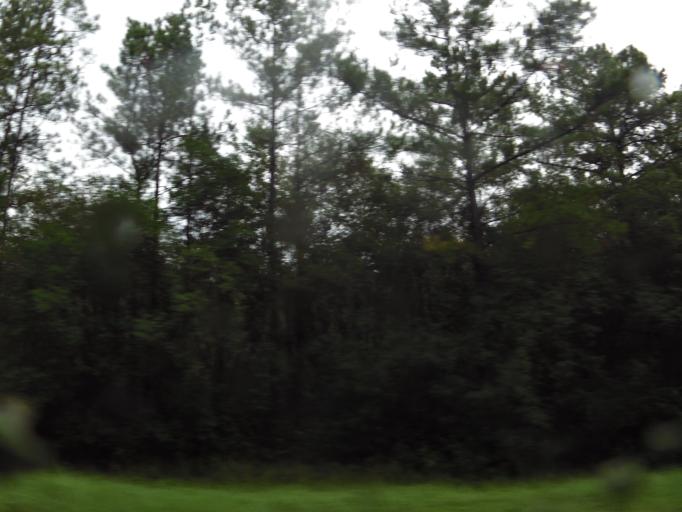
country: US
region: Georgia
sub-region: Wayne County
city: Jesup
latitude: 31.5442
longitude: -81.8601
